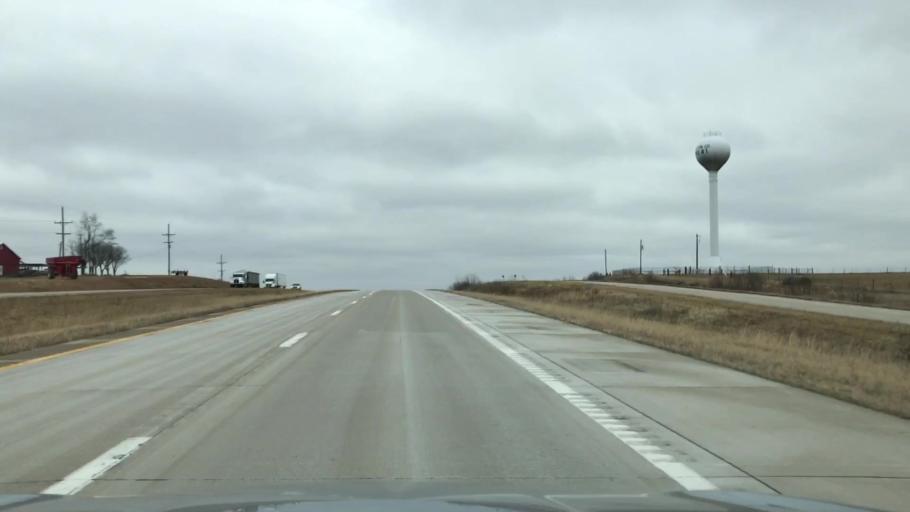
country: US
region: Missouri
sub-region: Livingston County
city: Chillicothe
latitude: 39.7393
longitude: -93.6608
